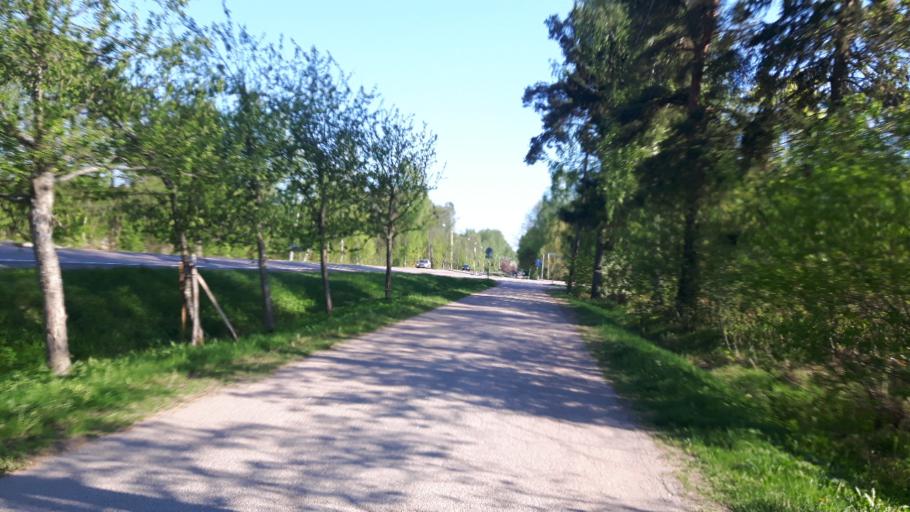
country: FI
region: Kymenlaakso
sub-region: Kotka-Hamina
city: Kotka
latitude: 60.4583
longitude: 26.8878
